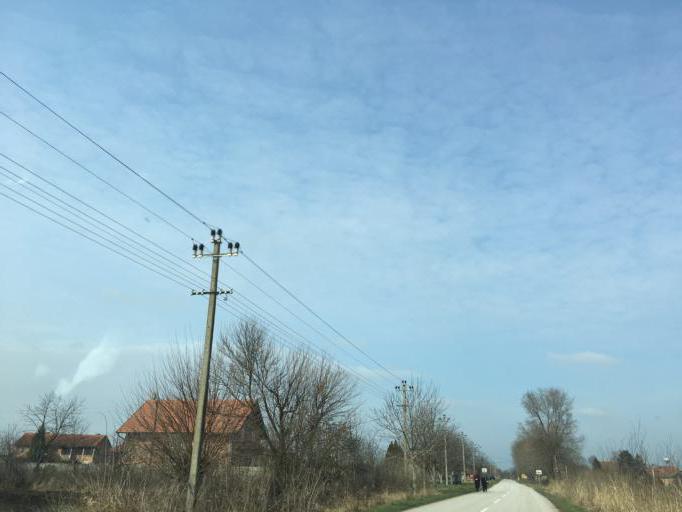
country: RS
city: Centa
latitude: 45.0987
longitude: 20.4028
